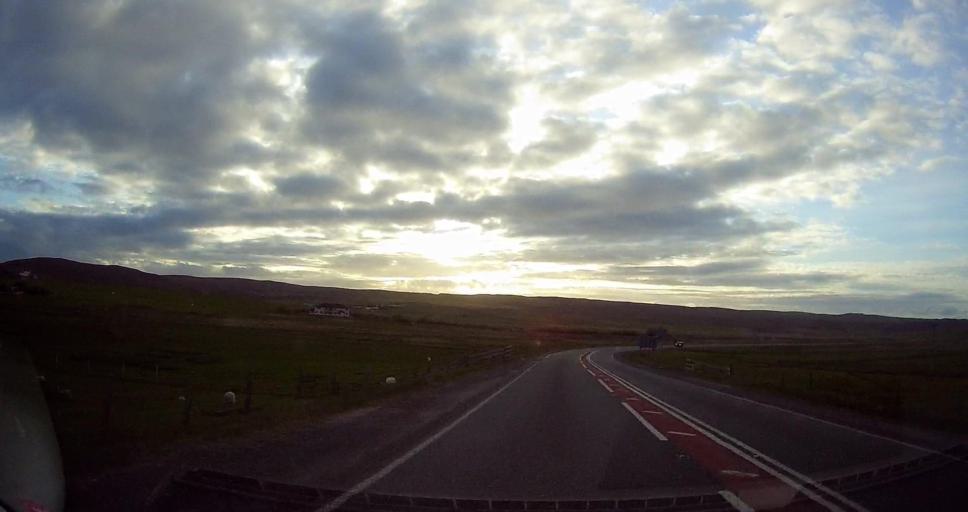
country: GB
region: Scotland
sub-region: Shetland Islands
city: Lerwick
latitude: 60.1868
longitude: -1.2278
